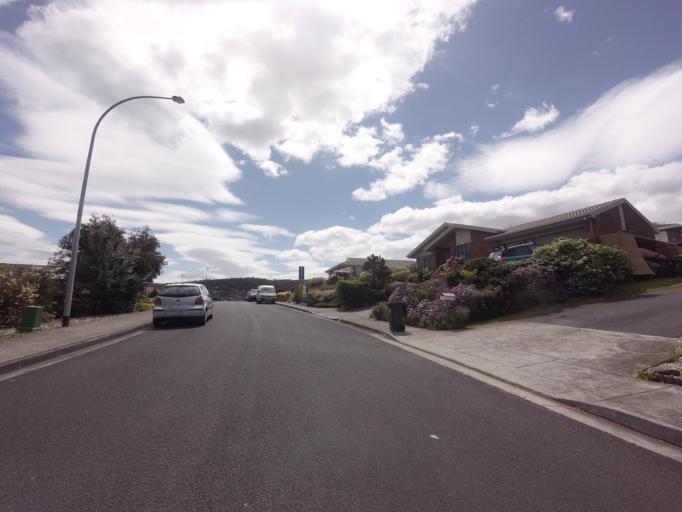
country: AU
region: Tasmania
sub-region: Clarence
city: Howrah
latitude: -42.8867
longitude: 147.4092
